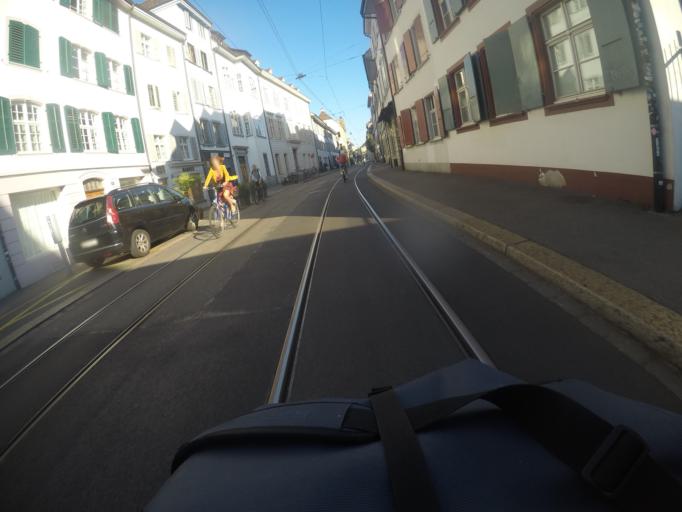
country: CH
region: Basel-City
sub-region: Basel-Stadt
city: Basel
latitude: 47.5627
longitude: 7.5851
